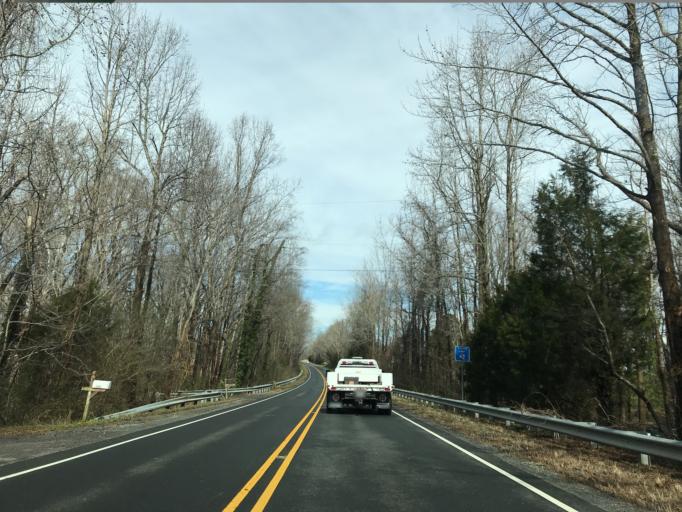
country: US
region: Virginia
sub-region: King George County
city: Dahlgren
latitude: 38.3212
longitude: -77.0803
